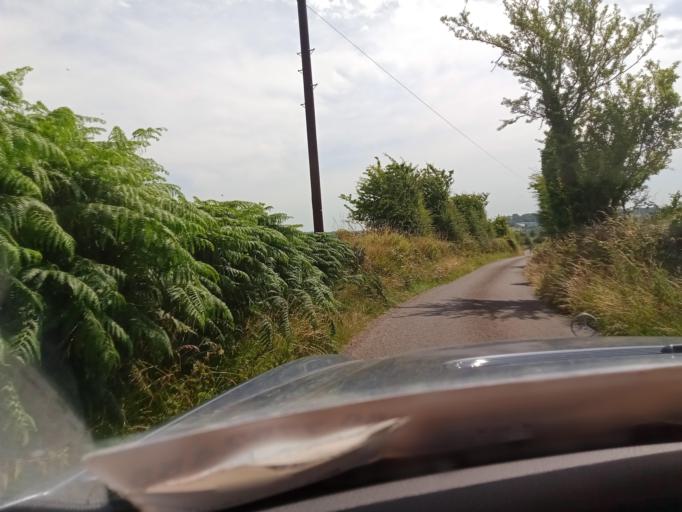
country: IE
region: Leinster
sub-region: Kilkenny
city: Mooncoin
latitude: 52.2621
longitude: -7.2027
